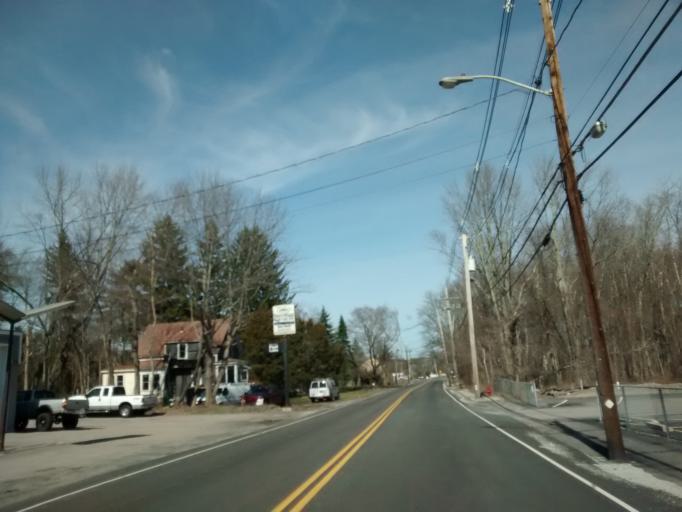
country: US
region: Massachusetts
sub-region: Norfolk County
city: Bellingham
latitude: 42.1309
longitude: -71.4499
